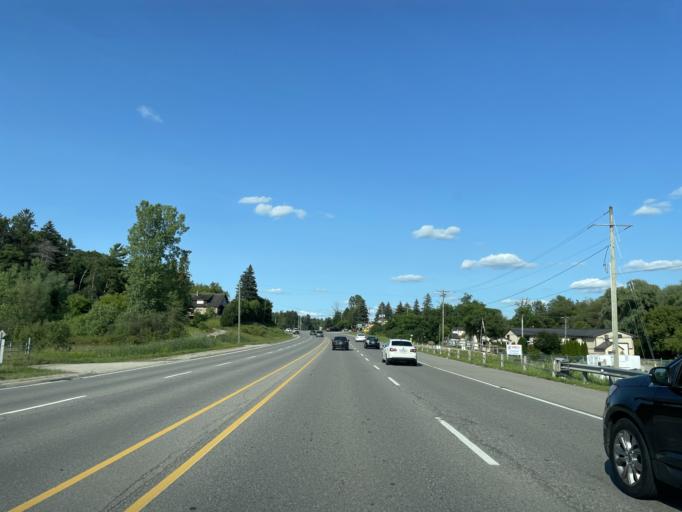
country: CA
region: Ontario
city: Waterloo
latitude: 43.4799
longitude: -80.4217
